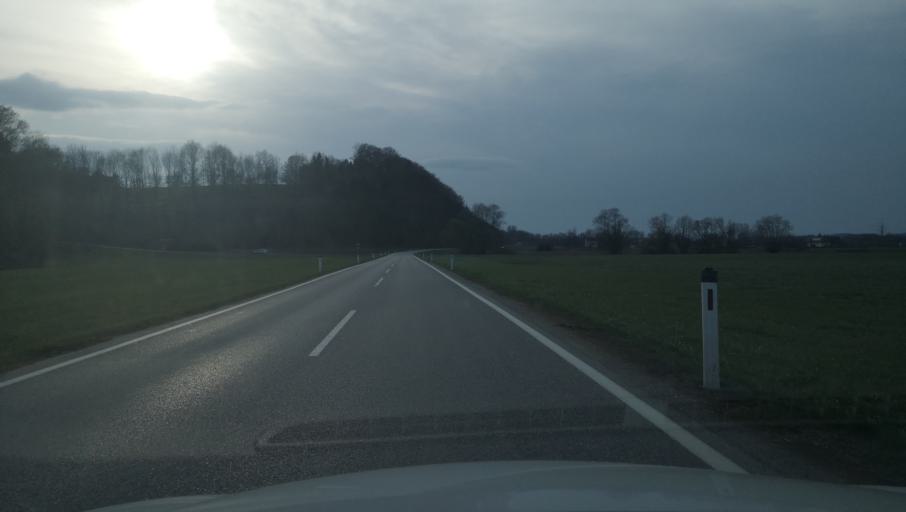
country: AT
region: Lower Austria
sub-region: Politischer Bezirk Amstetten
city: Euratsfeld
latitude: 48.0982
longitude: 14.9170
